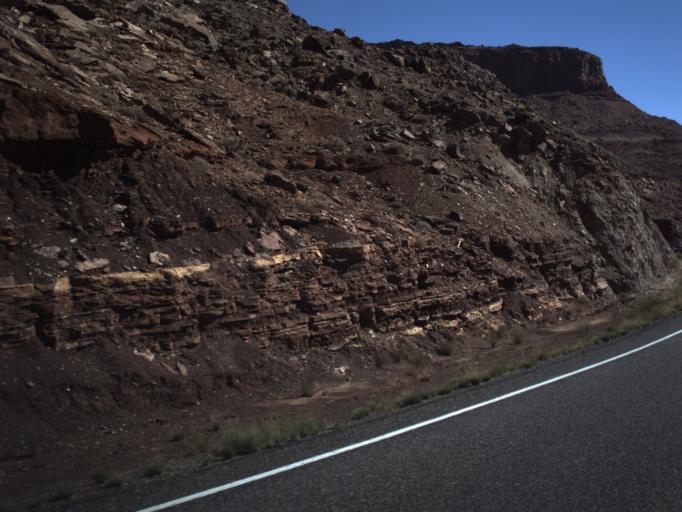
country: US
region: Utah
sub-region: San Juan County
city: Blanding
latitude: 37.8942
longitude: -110.4447
